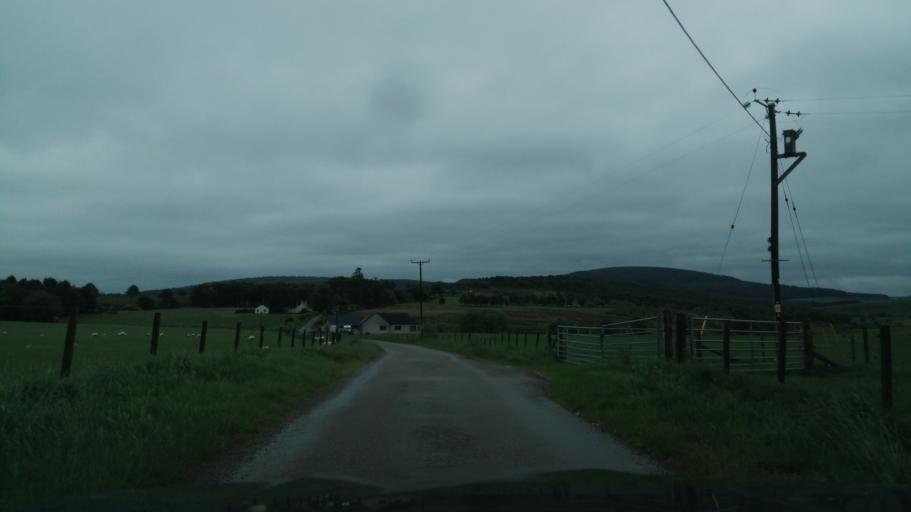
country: GB
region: Scotland
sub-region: Moray
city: Keith
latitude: 57.5709
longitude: -2.8615
